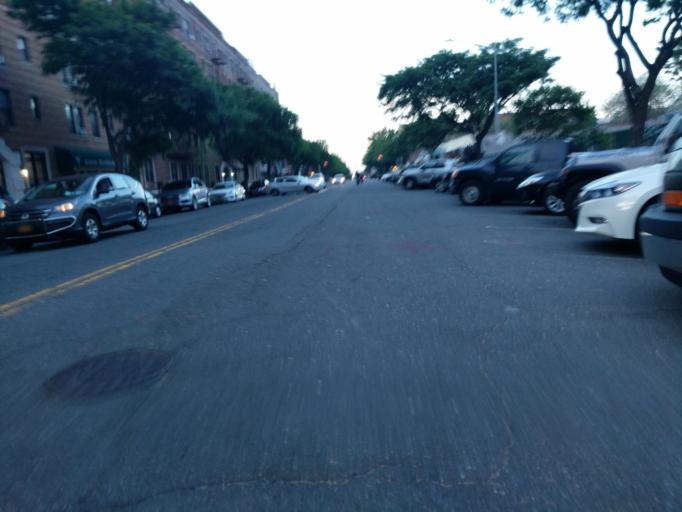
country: US
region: New York
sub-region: Queens County
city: Long Island City
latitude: 40.7771
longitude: -73.9095
